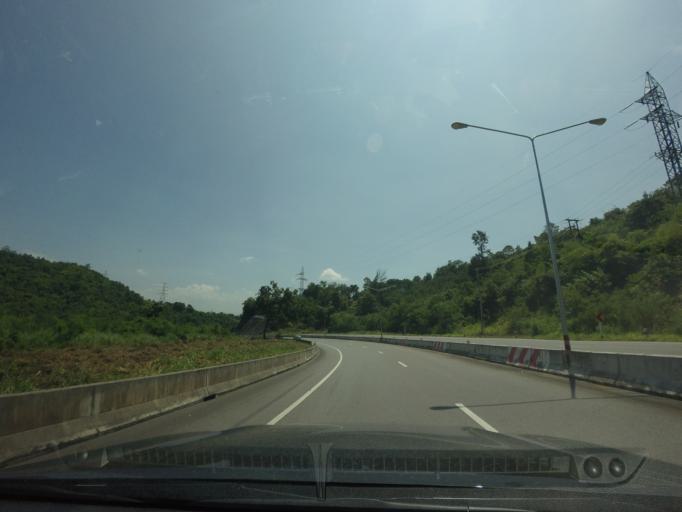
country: TH
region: Phetchabun
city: Lom Sak
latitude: 16.7674
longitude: 101.1379
